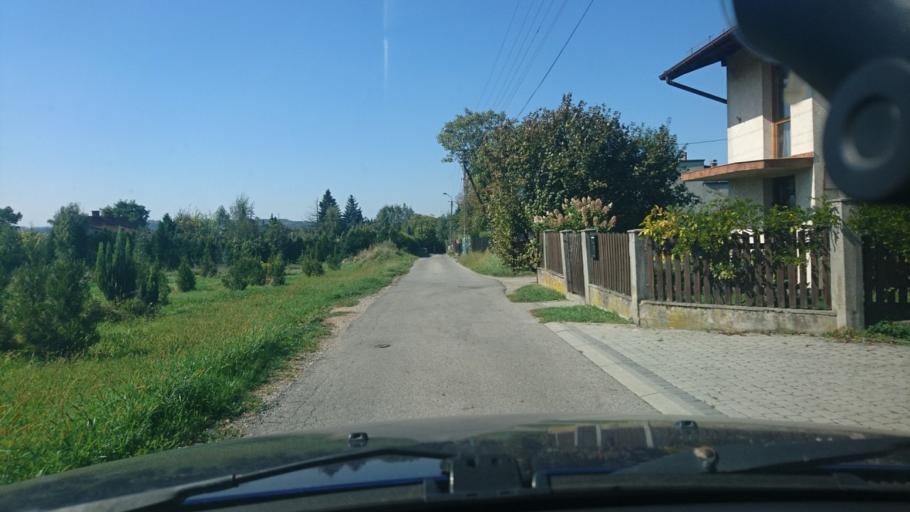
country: PL
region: Silesian Voivodeship
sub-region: Bielsko-Biala
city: Bielsko-Biala
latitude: 49.8416
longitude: 19.0615
